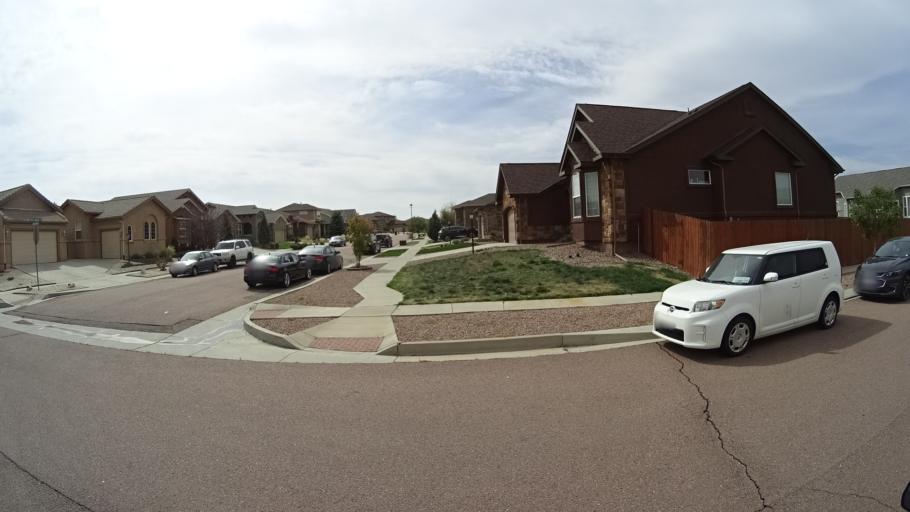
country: US
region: Colorado
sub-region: El Paso County
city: Cimarron Hills
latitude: 38.9226
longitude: -104.6931
